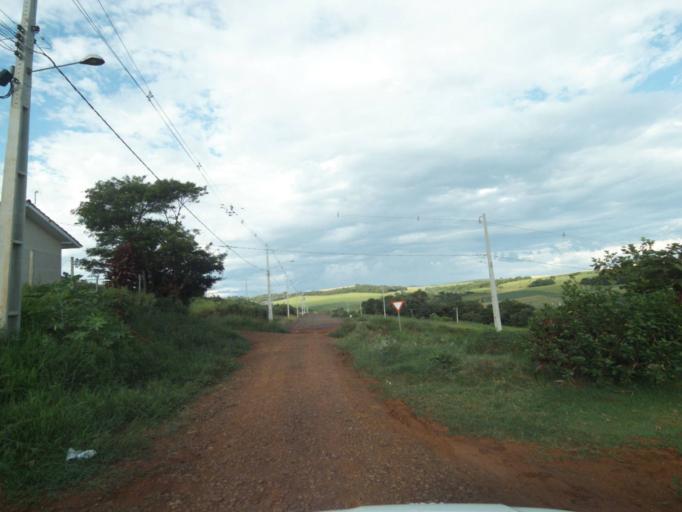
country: BR
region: Parana
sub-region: Laranjeiras Do Sul
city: Laranjeiras do Sul
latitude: -25.4910
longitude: -52.5241
